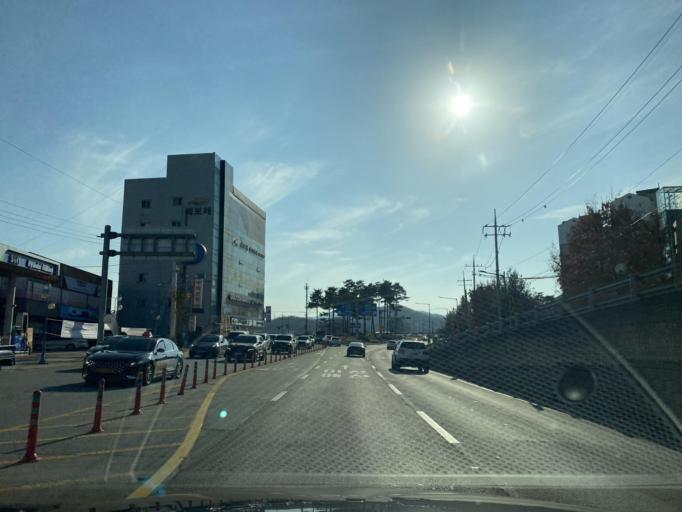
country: KR
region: Chungcheongnam-do
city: Cheonan
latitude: 36.7879
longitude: 127.1184
